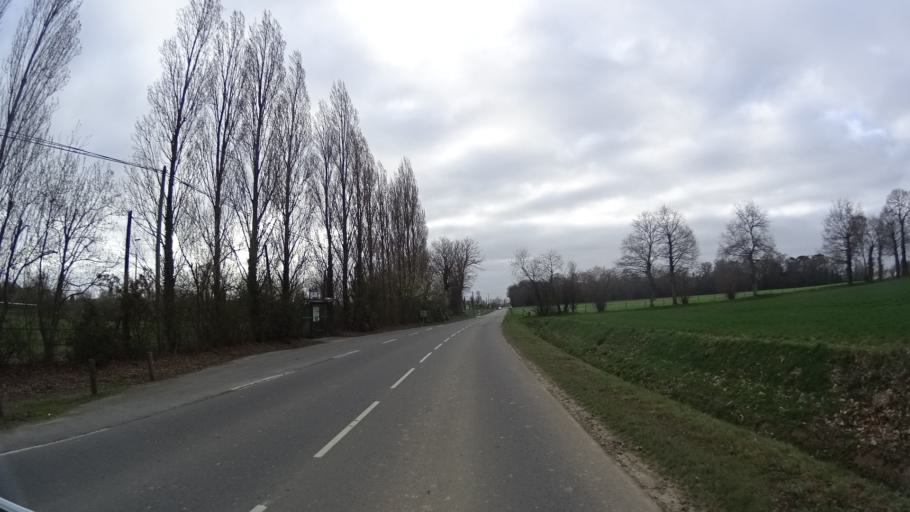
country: FR
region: Brittany
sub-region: Departement d'Ille-et-Vilaine
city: Saint-Gilles
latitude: 48.1811
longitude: -1.8509
